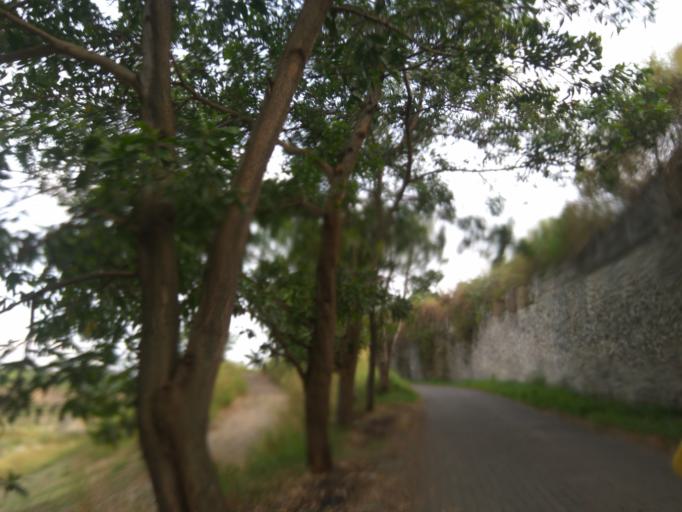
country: ID
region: Central Java
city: Semarang
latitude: -7.0254
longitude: 110.4428
